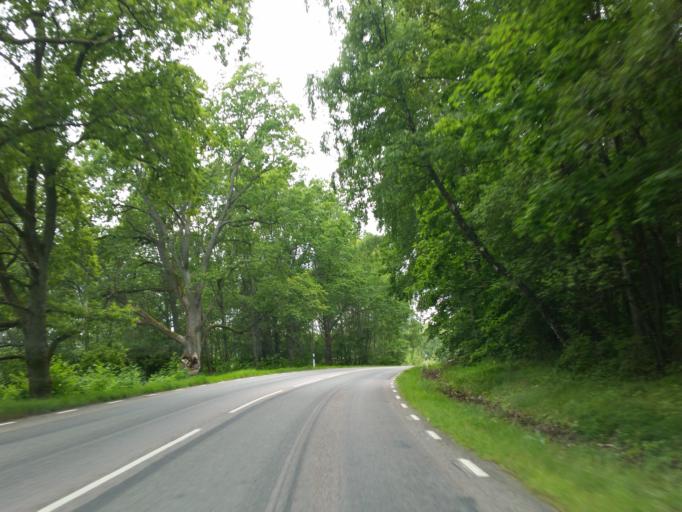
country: SE
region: Stockholm
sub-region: Sodertalje Kommun
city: Soedertaelje
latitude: 59.2019
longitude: 17.5555
